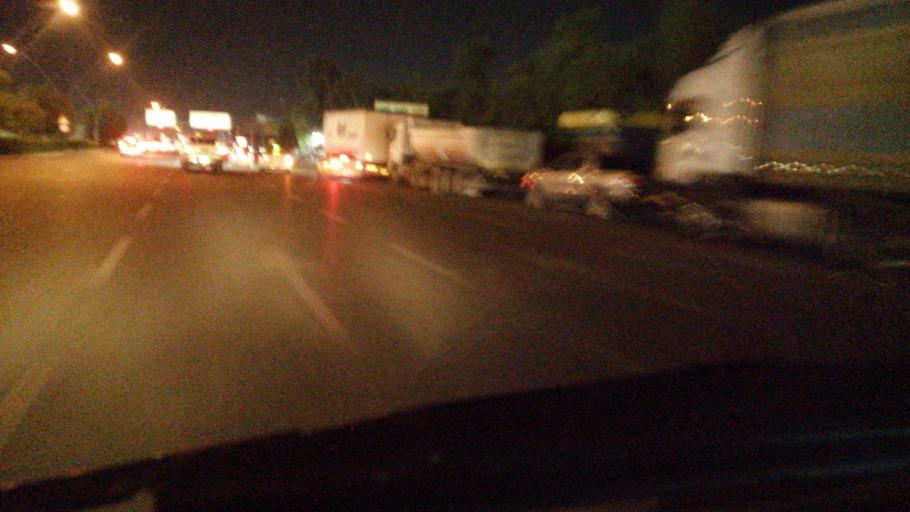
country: IQ
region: Arbil
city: Erbil
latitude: 36.1587
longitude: 43.9924
